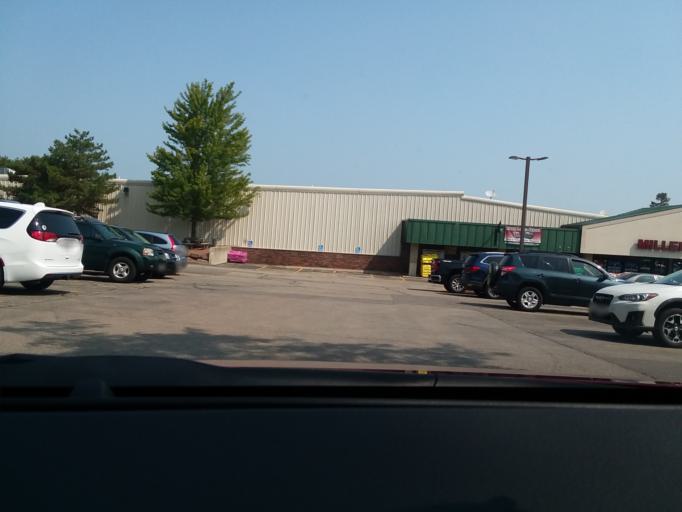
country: US
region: Wisconsin
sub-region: Dane County
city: Verona
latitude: 42.9883
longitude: -89.5341
